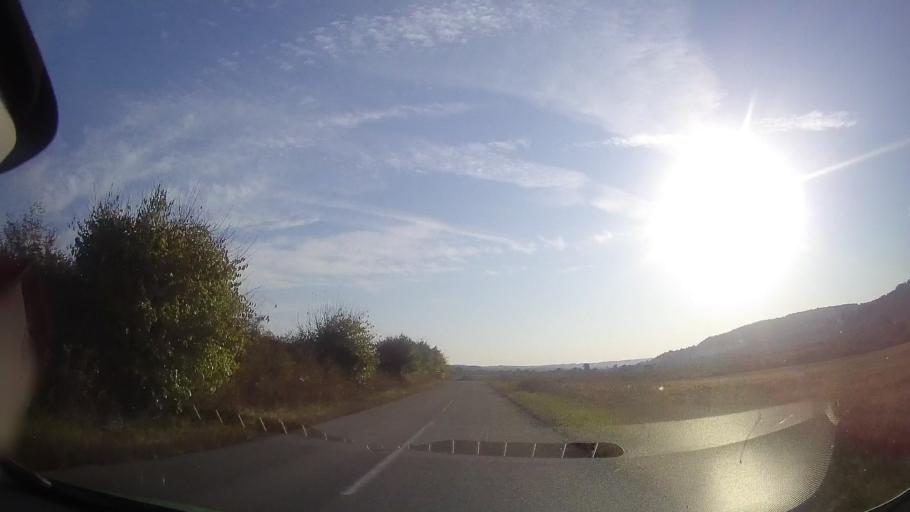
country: RO
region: Timis
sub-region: Comuna Bogda
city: Bogda
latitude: 45.9816
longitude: 21.5379
